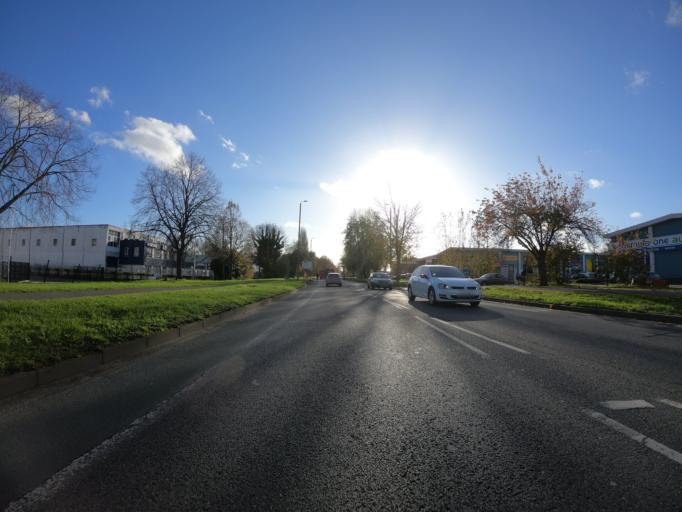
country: GB
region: England
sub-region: Greater London
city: Orpington
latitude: 51.3895
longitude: 0.1100
